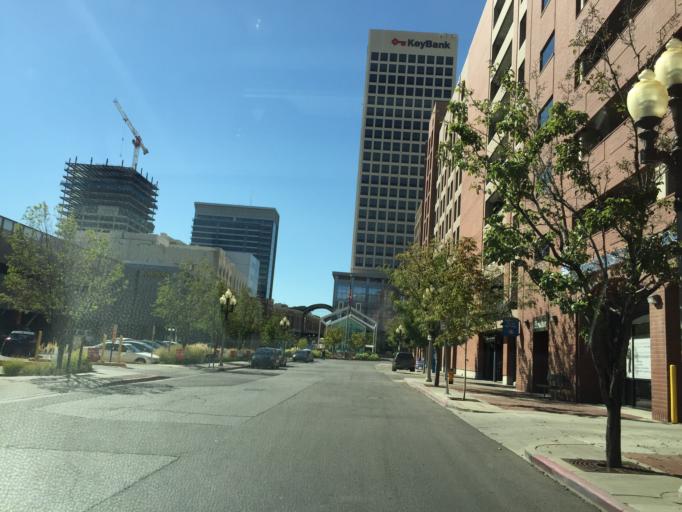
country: US
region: Utah
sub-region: Salt Lake County
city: Salt Lake City
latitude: 40.7682
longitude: -111.8863
